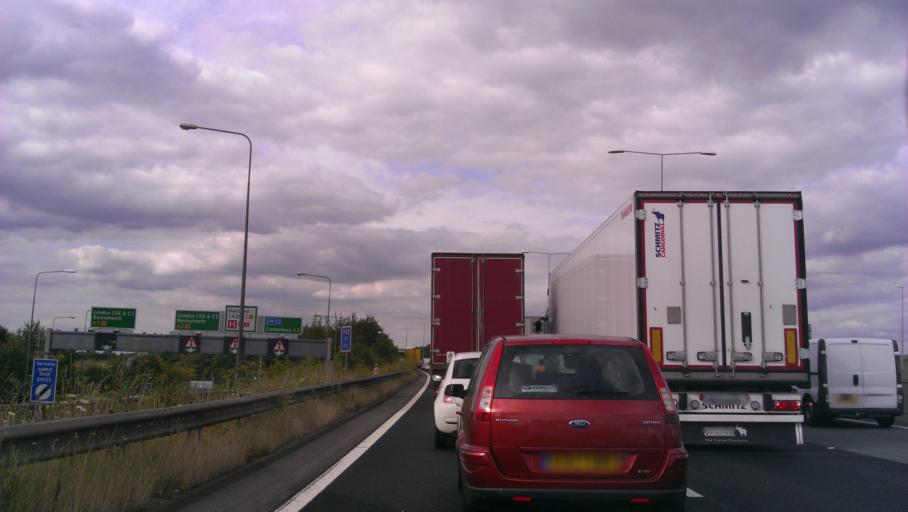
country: GB
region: England
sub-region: Kent
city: Dartford
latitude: 51.4239
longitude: 0.2367
